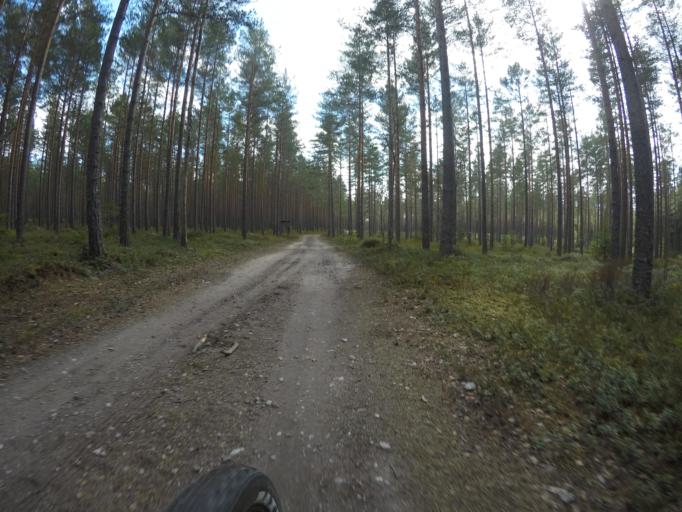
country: SE
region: Vaestmanland
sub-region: Kungsors Kommun
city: Kungsoer
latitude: 59.3621
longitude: 16.1085
